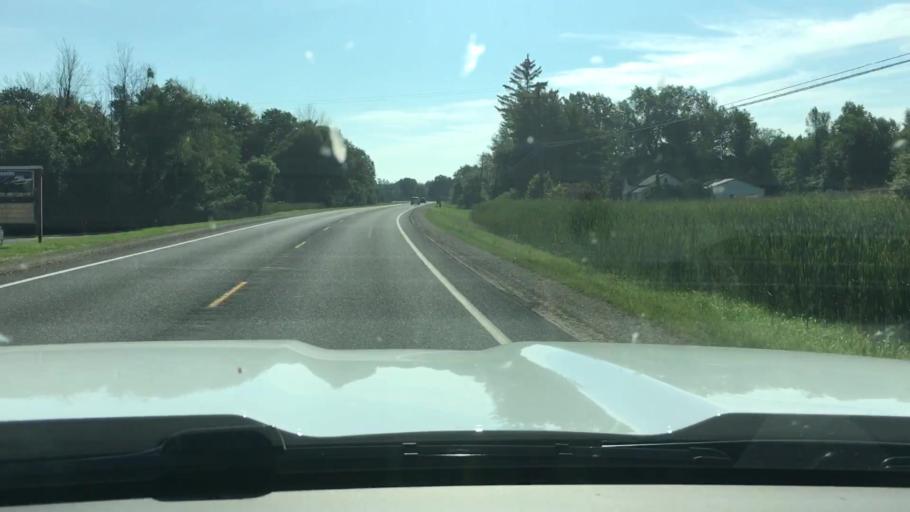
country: US
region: Michigan
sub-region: Montcalm County
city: Edmore
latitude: 43.4077
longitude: -84.9816
